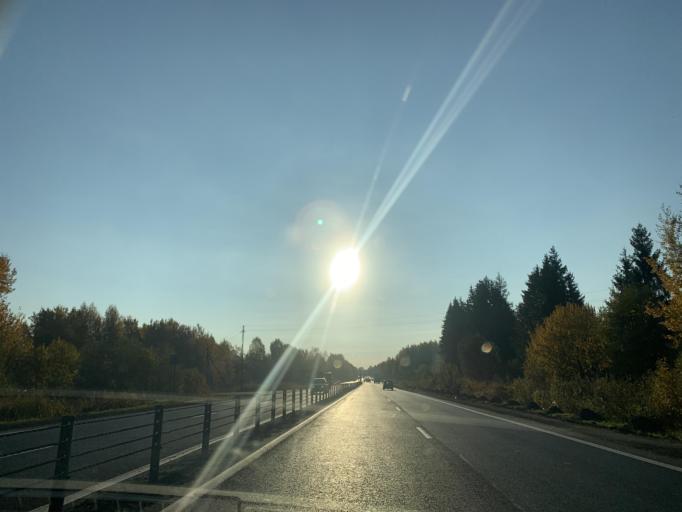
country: RU
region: Jaroslavl
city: Konstantinovskiy
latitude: 57.7850
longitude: 39.6193
